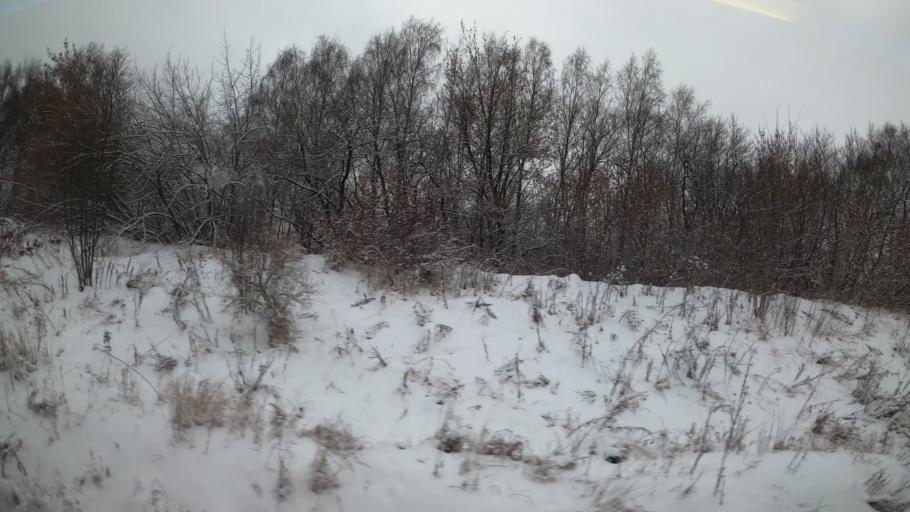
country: RU
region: Jaroslavl
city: Pereslavl'-Zalesskiy
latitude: 56.6817
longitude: 38.9193
